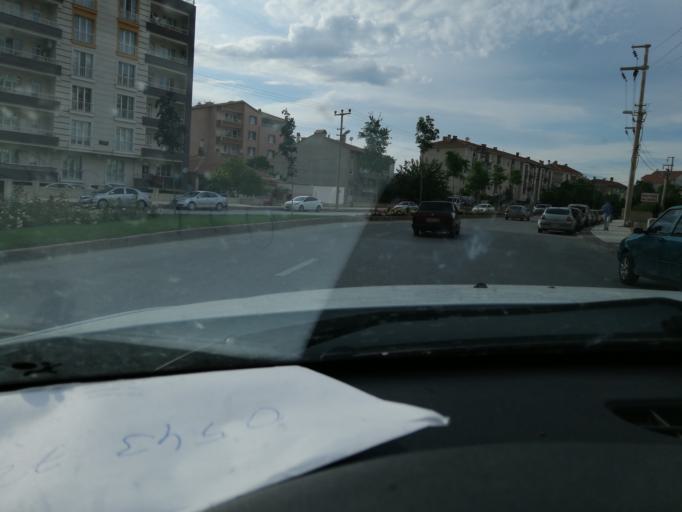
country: TR
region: Kirsehir
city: Kirsehir
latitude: 39.1355
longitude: 34.1597
